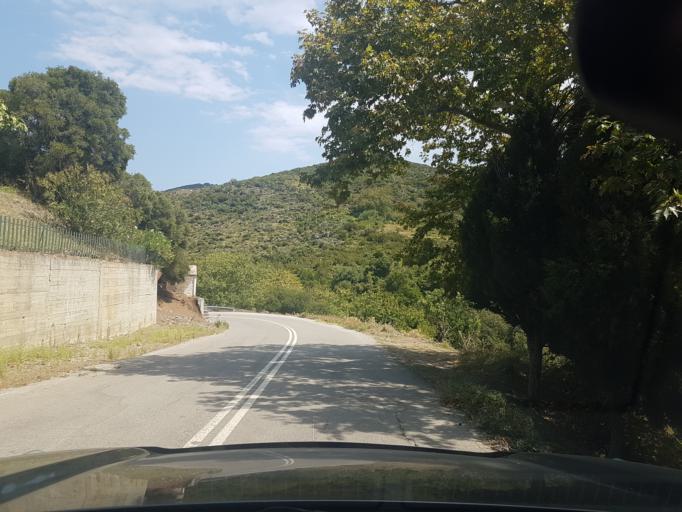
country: GR
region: Central Greece
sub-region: Nomos Evvoias
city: Kymi
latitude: 38.6355
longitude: 24.0751
